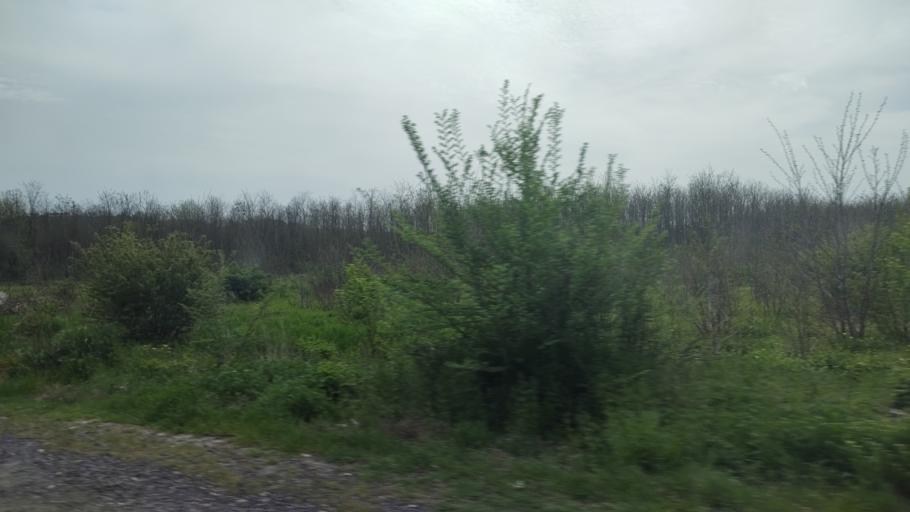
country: RO
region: Constanta
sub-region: Oras Murfatlar
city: Murfatlar
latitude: 44.1698
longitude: 28.3977
